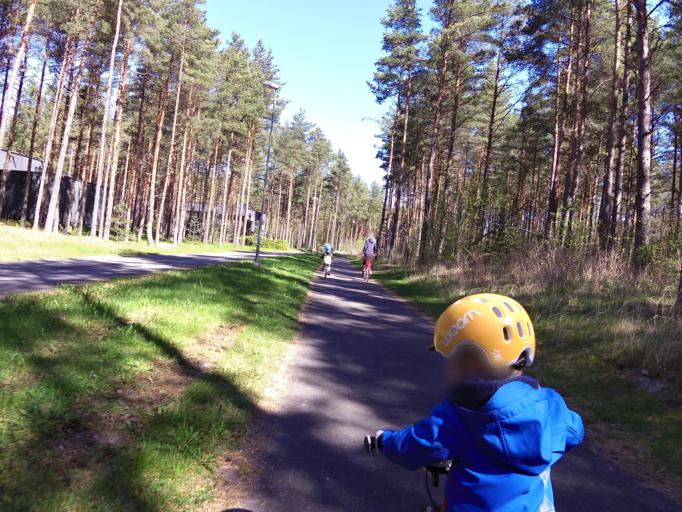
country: EE
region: Harju
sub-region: Raasiku vald
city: Raasiku
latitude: 59.4926
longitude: 25.1759
